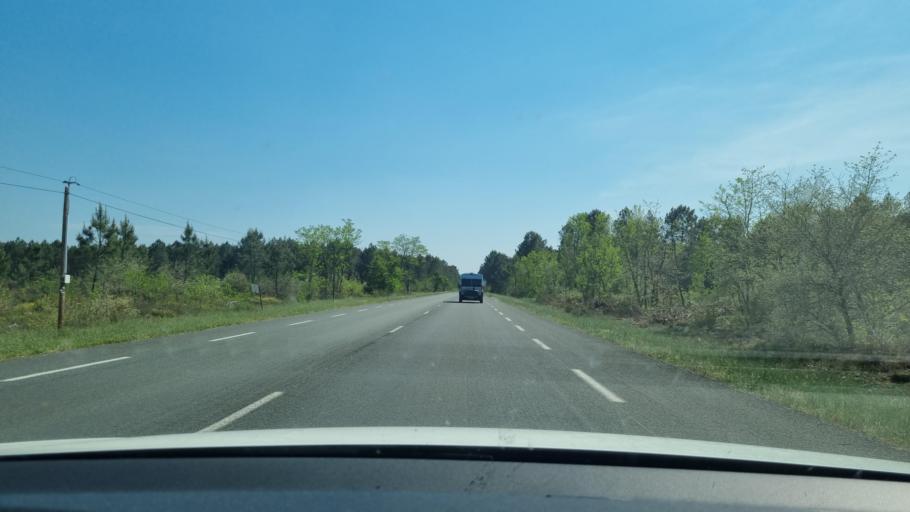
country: FR
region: Aquitaine
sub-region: Departement de la Gironde
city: Prechac
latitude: 44.2755
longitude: -0.2618
